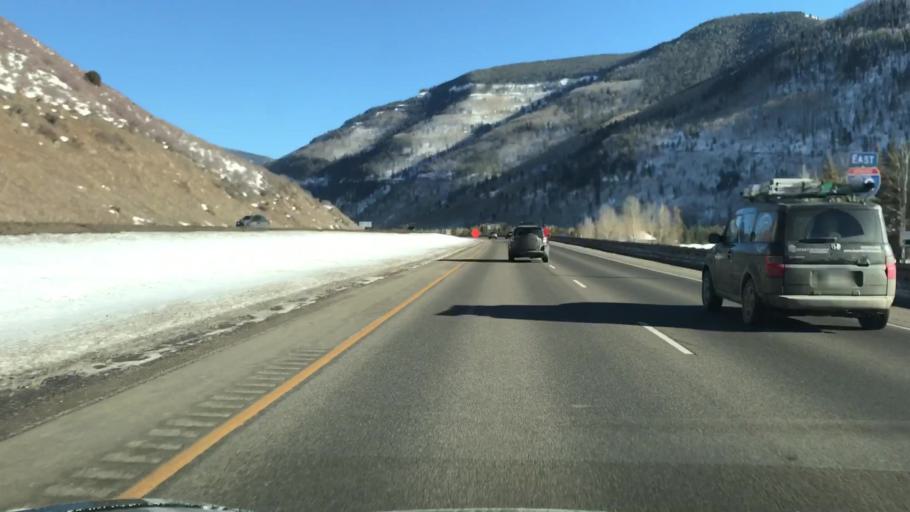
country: US
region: Colorado
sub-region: Eagle County
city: Vail
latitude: 39.6420
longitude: -106.3686
